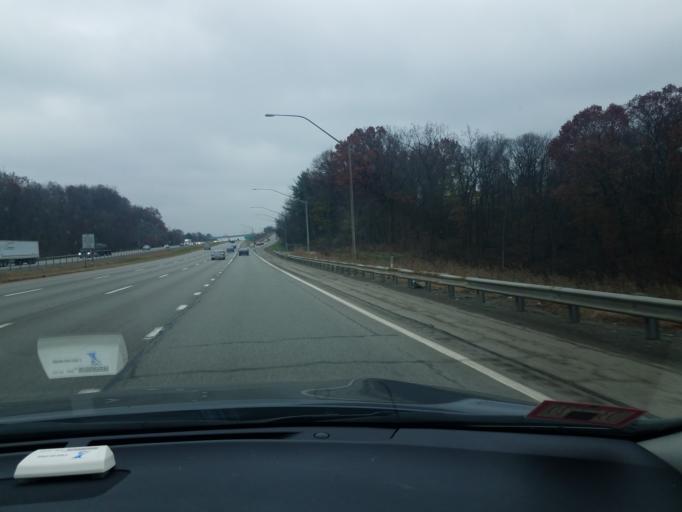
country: US
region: Pennsylvania
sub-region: Allegheny County
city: Bradford Woods
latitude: 40.6236
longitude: -80.0968
